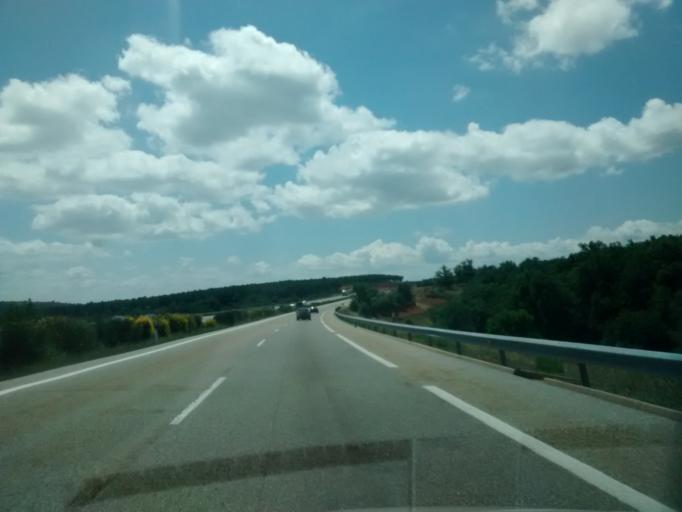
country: ES
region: Castille and Leon
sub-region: Provincia de Leon
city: Brazuelo
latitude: 42.5146
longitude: -6.1175
